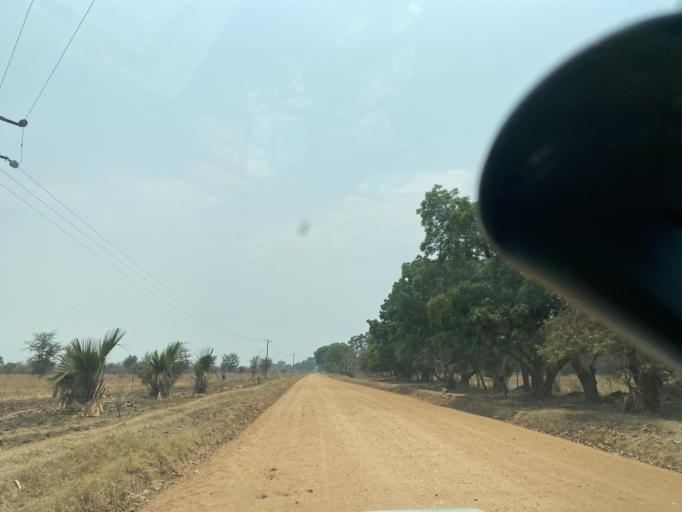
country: ZM
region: Lusaka
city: Kafue
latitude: -15.6208
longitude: 28.1008
